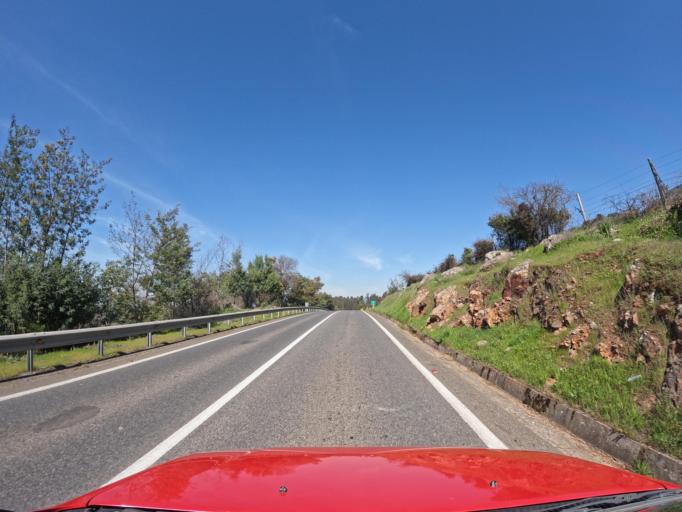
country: CL
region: Maule
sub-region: Provincia de Curico
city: Rauco
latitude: -35.0665
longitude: -71.6237
